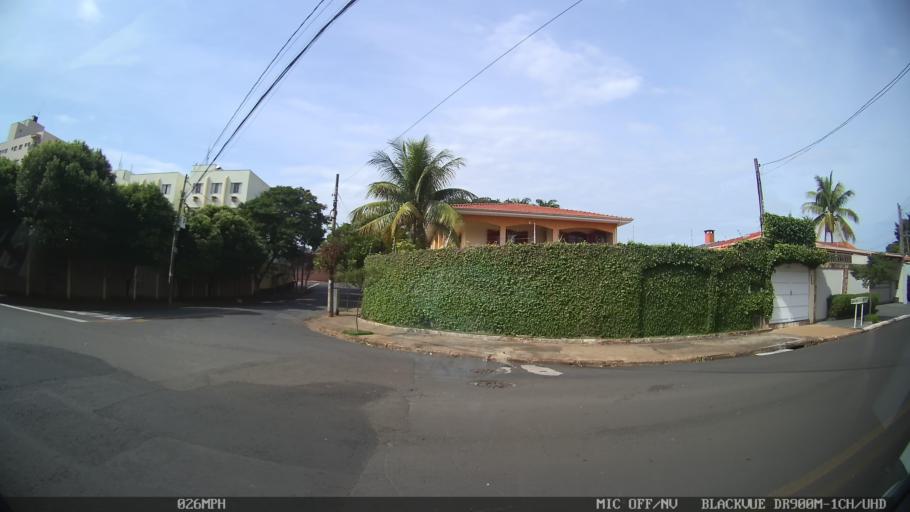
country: BR
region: Sao Paulo
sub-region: Piracicaba
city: Piracicaba
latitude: -22.7073
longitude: -47.6723
